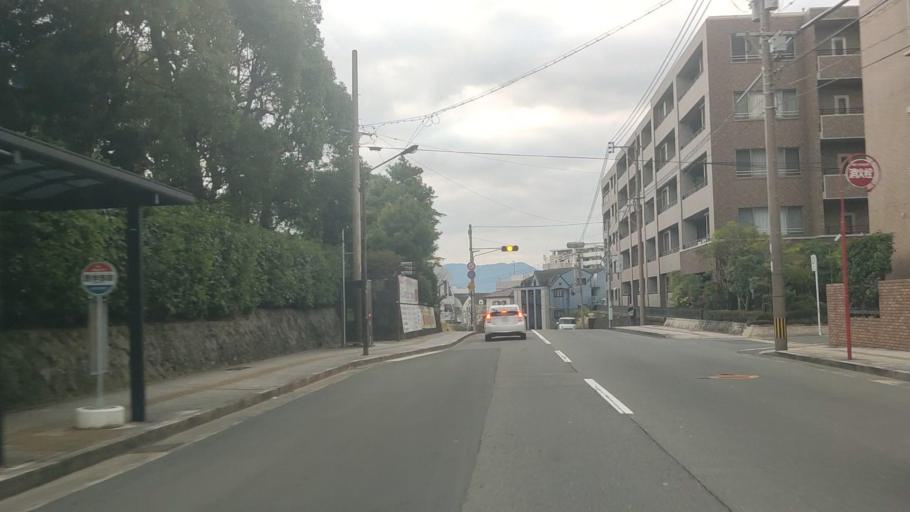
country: JP
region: Nagasaki
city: Nagasaki-shi
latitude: 32.7728
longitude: 129.8672
